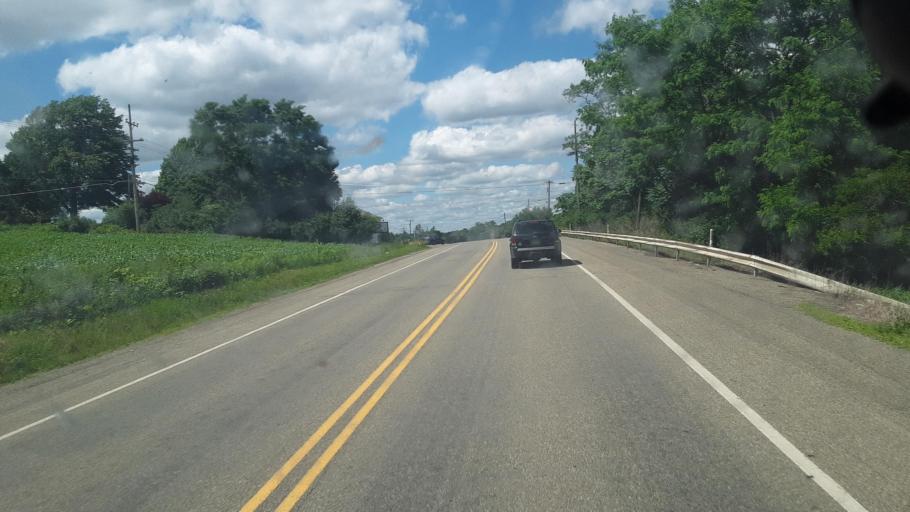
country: US
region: Pennsylvania
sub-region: Butler County
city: Prospect
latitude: 40.9555
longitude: -80.1547
